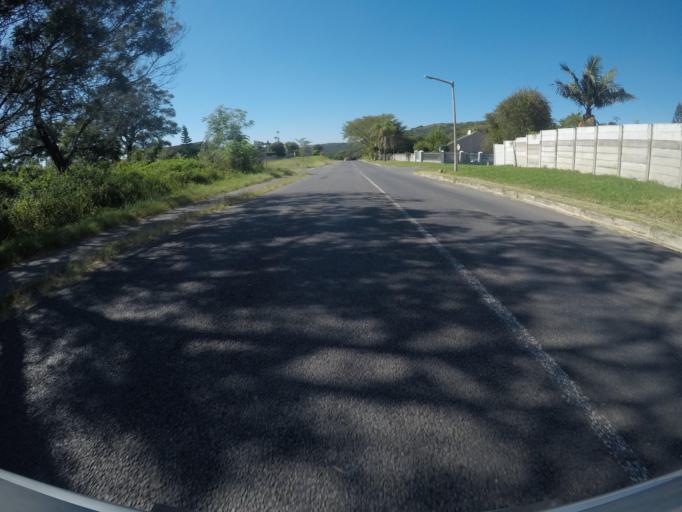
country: ZA
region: Eastern Cape
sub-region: Buffalo City Metropolitan Municipality
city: East London
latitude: -32.9494
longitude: 27.9031
